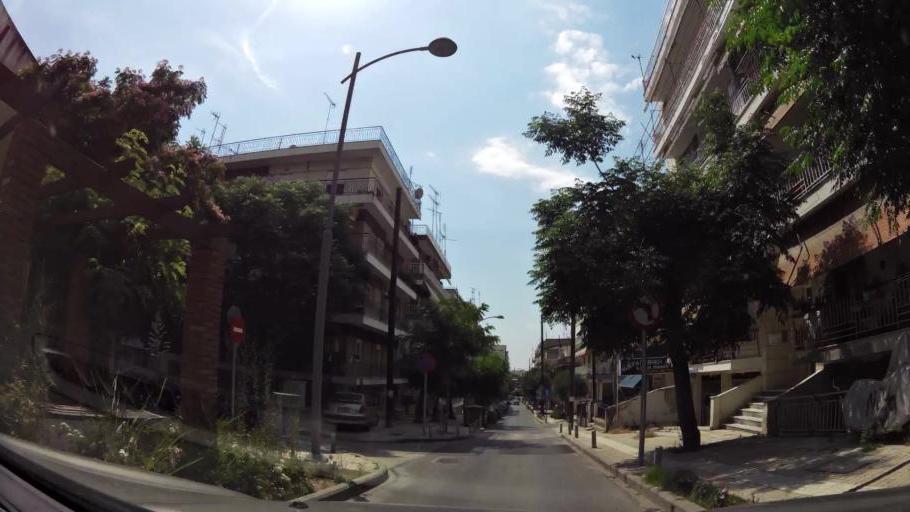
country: GR
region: Central Macedonia
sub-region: Nomos Thessalonikis
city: Stavroupoli
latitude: 40.6644
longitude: 22.9389
